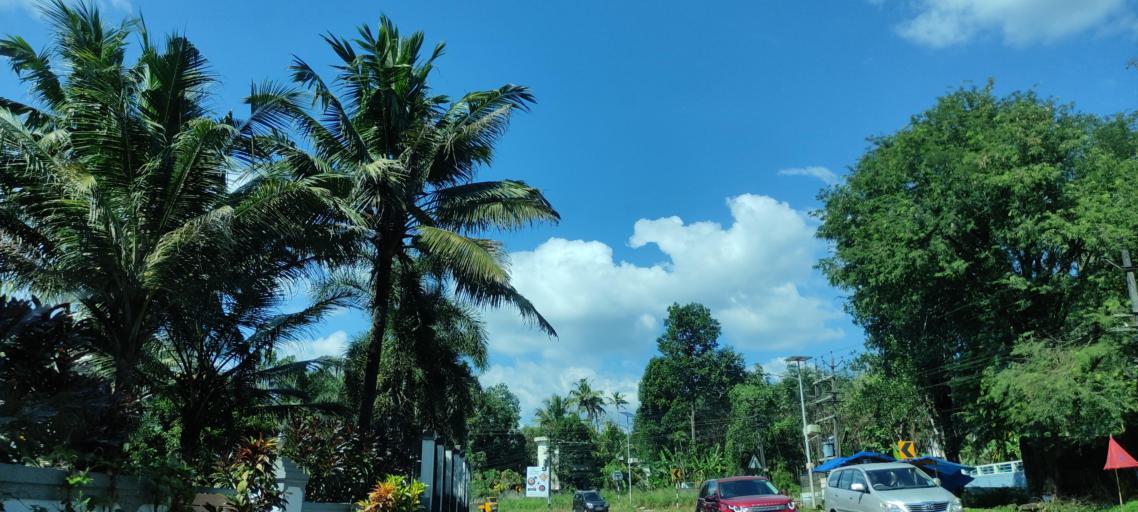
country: IN
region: Kerala
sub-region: Pattanamtitta
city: Adur
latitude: 9.1411
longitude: 76.7344
